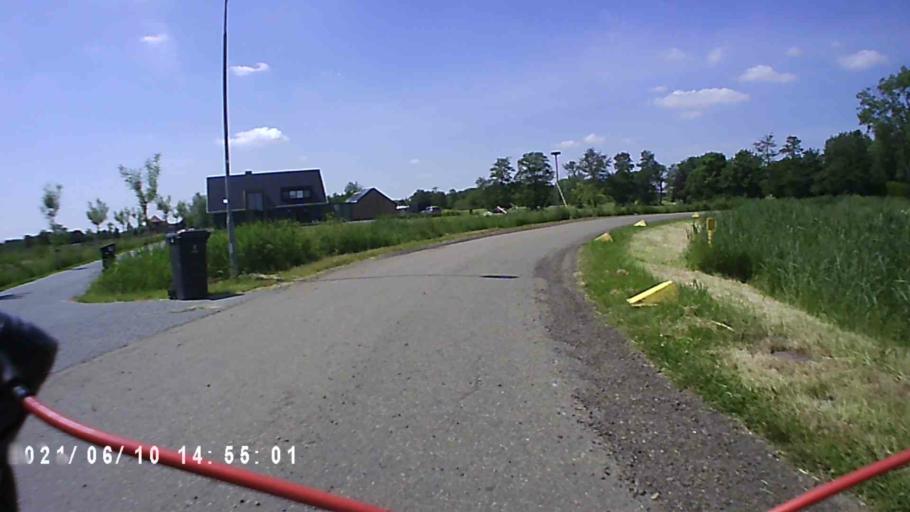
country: NL
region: Groningen
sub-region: Gemeente Grootegast
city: Grootegast
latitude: 53.2183
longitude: 6.2525
